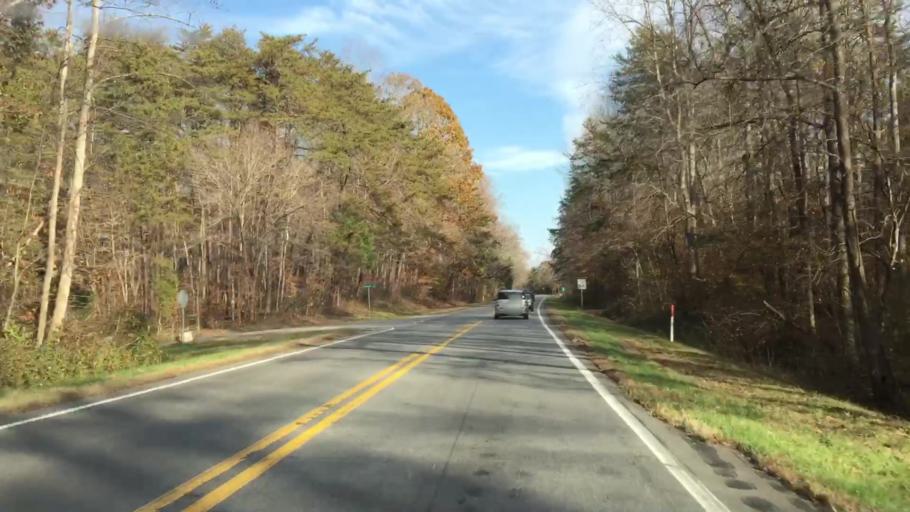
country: US
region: North Carolina
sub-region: Guilford County
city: Stokesdale
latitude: 36.2288
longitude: -80.0351
